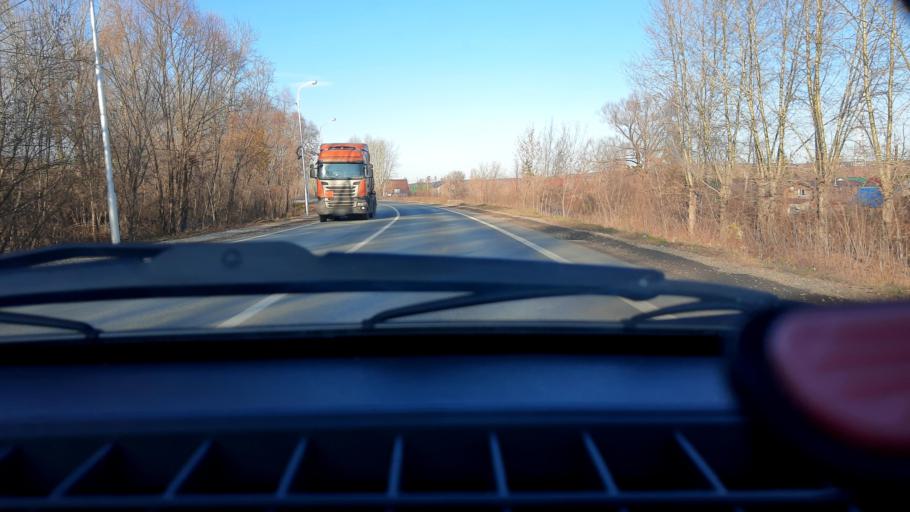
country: RU
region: Bashkortostan
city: Ufa
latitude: 54.8334
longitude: 56.1338
